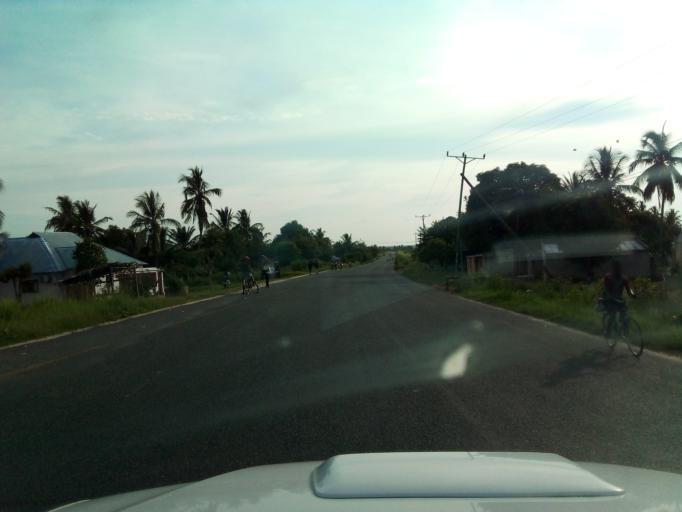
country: MZ
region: Zambezia
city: Quelimane
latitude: -17.4897
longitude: 37.0287
